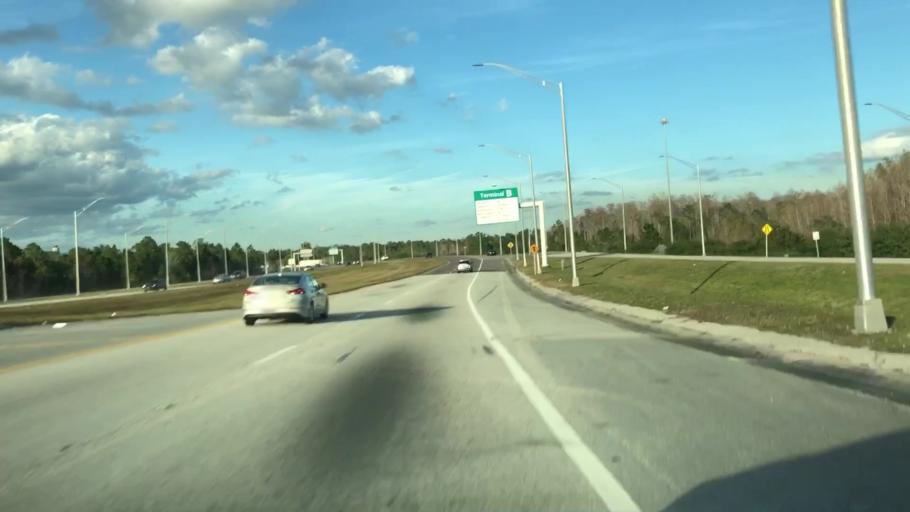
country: US
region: Florida
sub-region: Orange County
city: Meadow Woods
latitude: 28.3993
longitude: -81.3090
